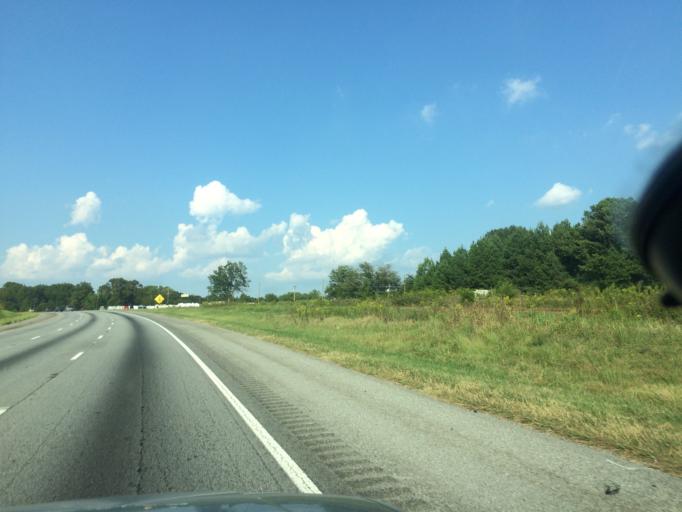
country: US
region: South Carolina
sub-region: Anderson County
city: Piedmont
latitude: 34.6924
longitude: -82.5050
